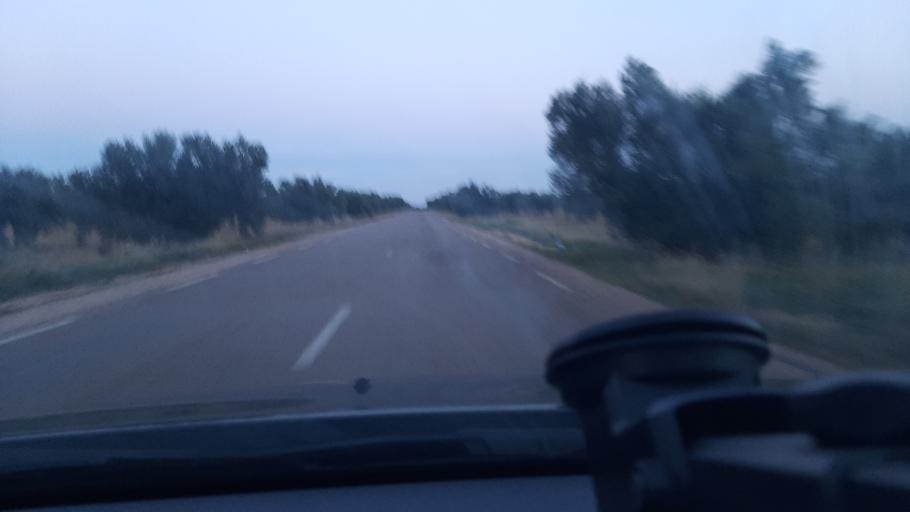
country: TN
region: Al Mahdiyah
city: Shurban
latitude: 35.0335
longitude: 10.5118
